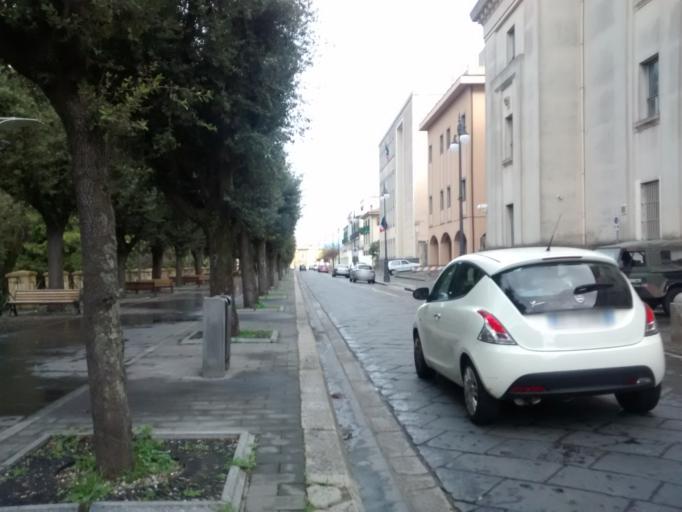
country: IT
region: Calabria
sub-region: Provincia di Vibo-Valentia
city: Vibo Valentia
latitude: 38.6748
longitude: 16.1060
